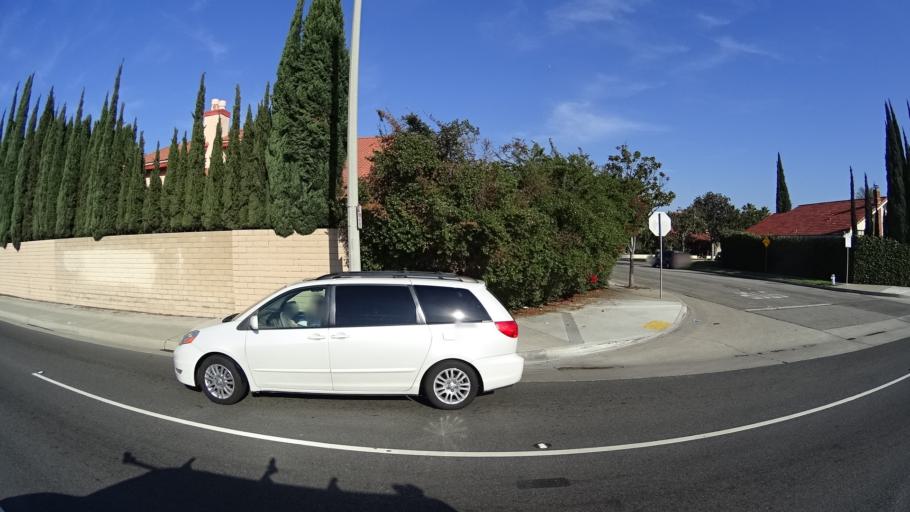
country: US
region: California
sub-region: Orange County
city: Fountain Valley
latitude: 33.7275
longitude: -117.9187
